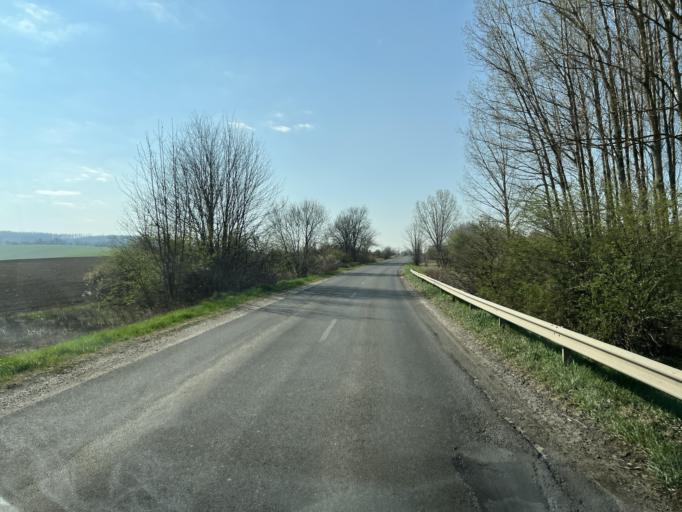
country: HU
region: Pest
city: Galgamacsa
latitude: 47.6954
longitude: 19.4015
